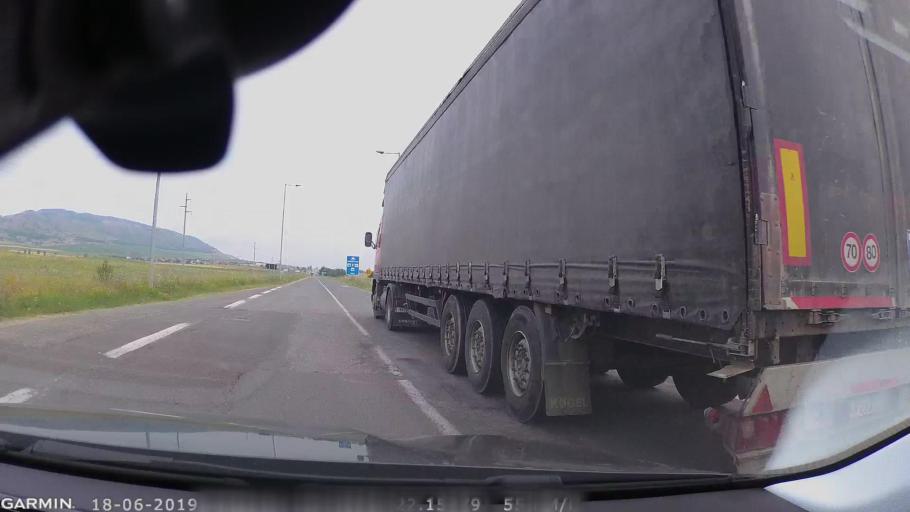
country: MK
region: Stip
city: Shtip
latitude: 41.7684
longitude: 22.1532
